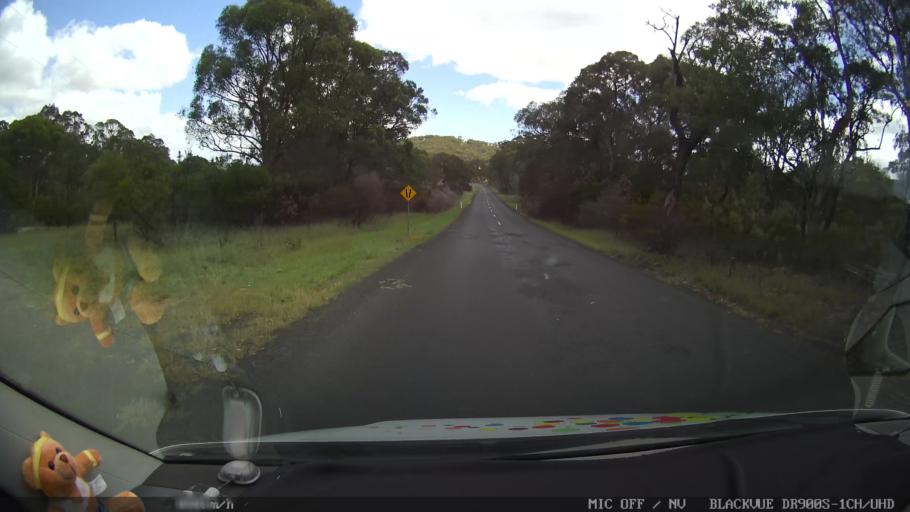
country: AU
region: New South Wales
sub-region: Glen Innes Severn
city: Glen Innes
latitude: -29.5407
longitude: 151.6709
